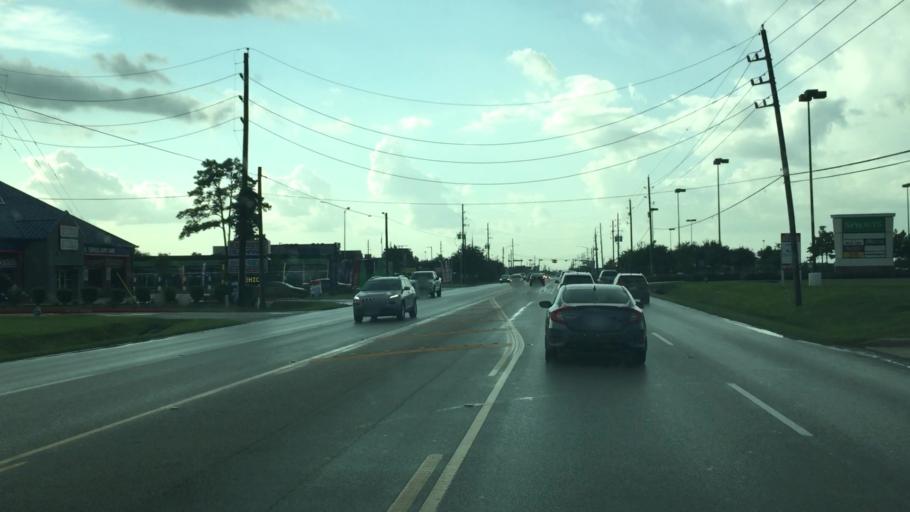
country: US
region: Texas
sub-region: Montgomery County
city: The Woodlands
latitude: 30.0687
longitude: -95.5077
